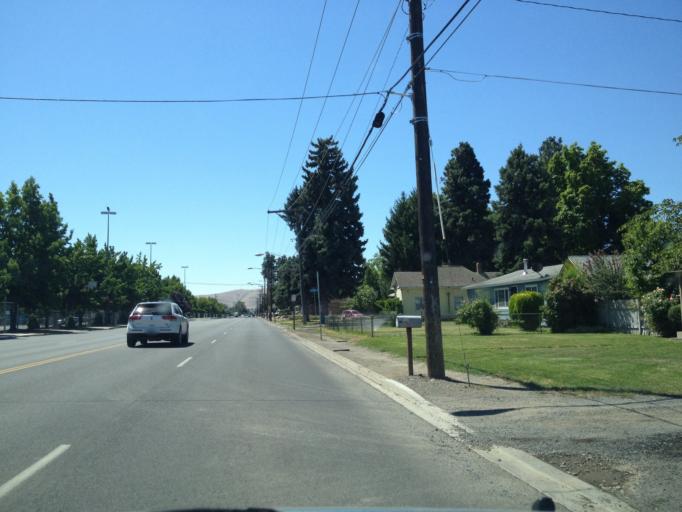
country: US
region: Washington
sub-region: Yakima County
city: Yakima
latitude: 46.5902
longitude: -120.4882
